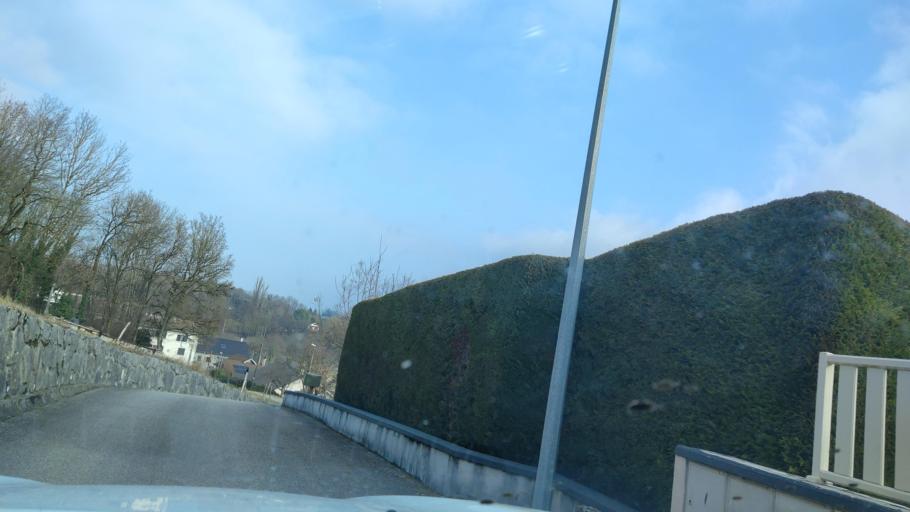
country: FR
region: Rhone-Alpes
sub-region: Departement de la Savoie
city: Gresy-sur-Aix
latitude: 45.7253
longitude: 5.9164
